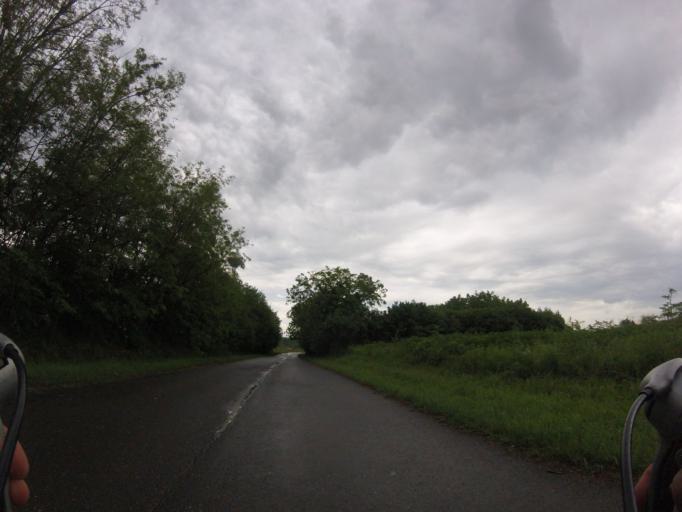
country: HU
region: Baranya
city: Pellerd
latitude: 45.9652
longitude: 18.1973
